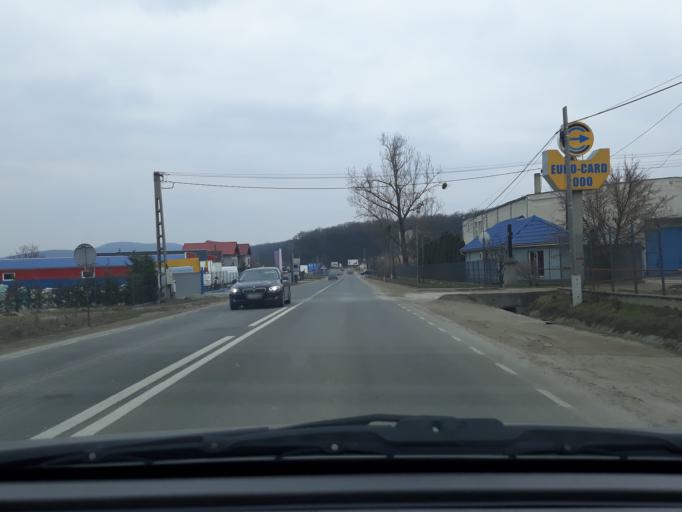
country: RO
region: Salaj
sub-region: Comuna Hereclean
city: Hereclean
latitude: 47.2276
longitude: 23.0036
